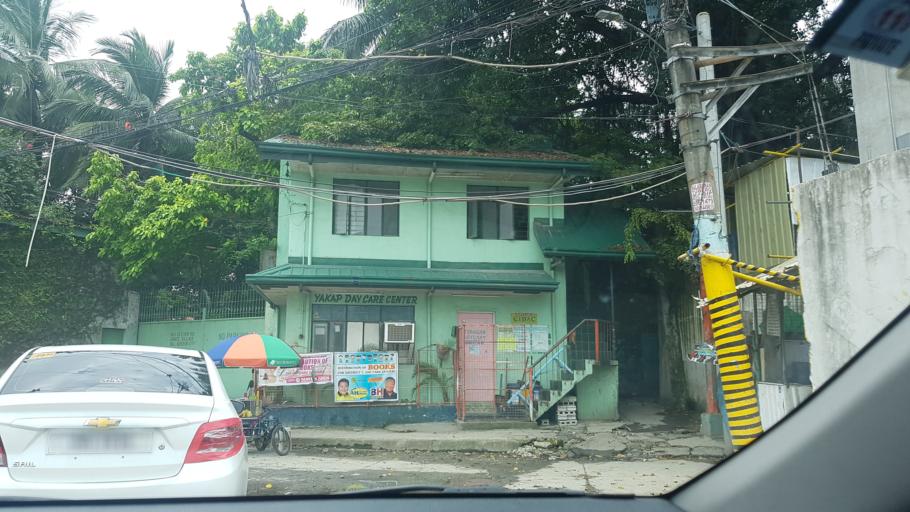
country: PH
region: Calabarzon
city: Del Monte
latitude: 14.6533
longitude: 121.0020
